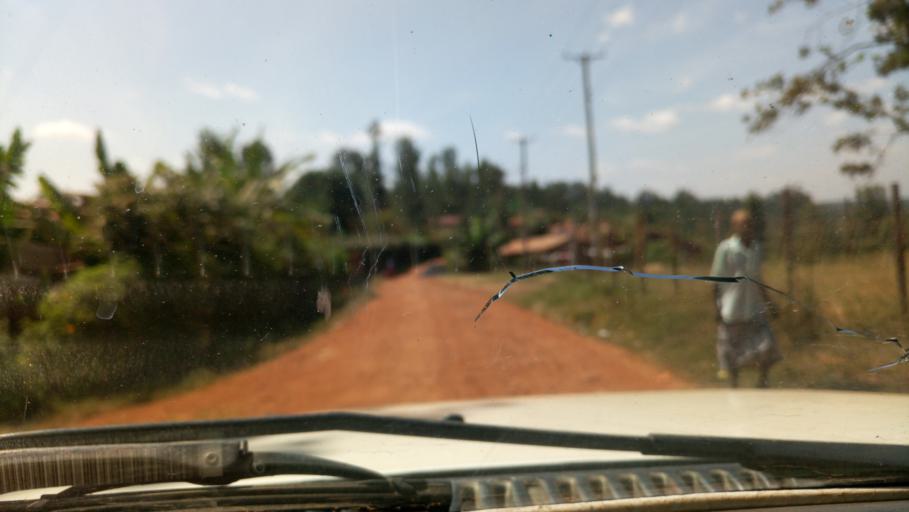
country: KE
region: Murang'a District
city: Murang'a
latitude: -0.7407
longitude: 37.1389
